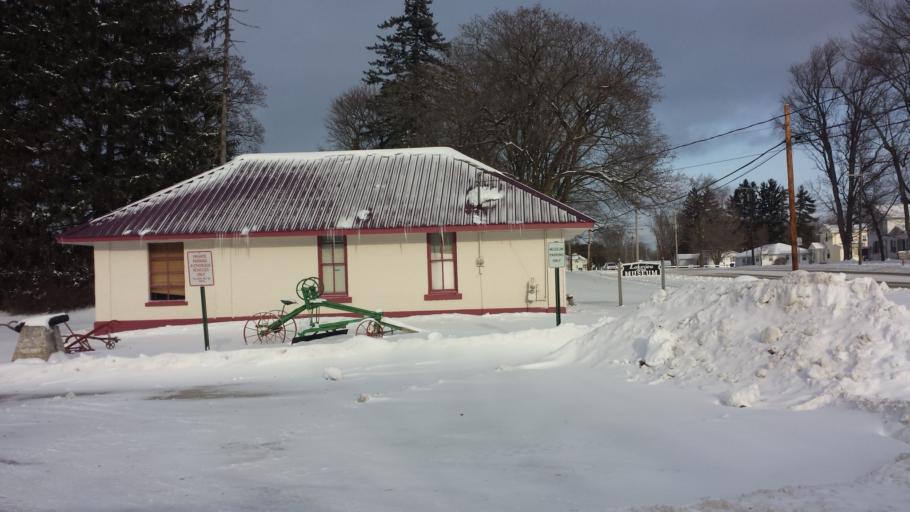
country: US
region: Michigan
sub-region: Montcalm County
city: Lakeview
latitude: 43.4440
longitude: -85.2816
